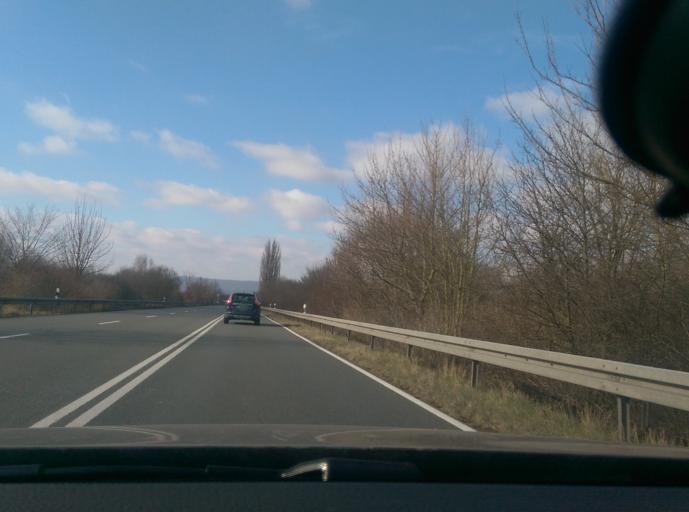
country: DE
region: Lower Saxony
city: Hessisch Oldendorf
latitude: 52.1482
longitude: 9.2851
